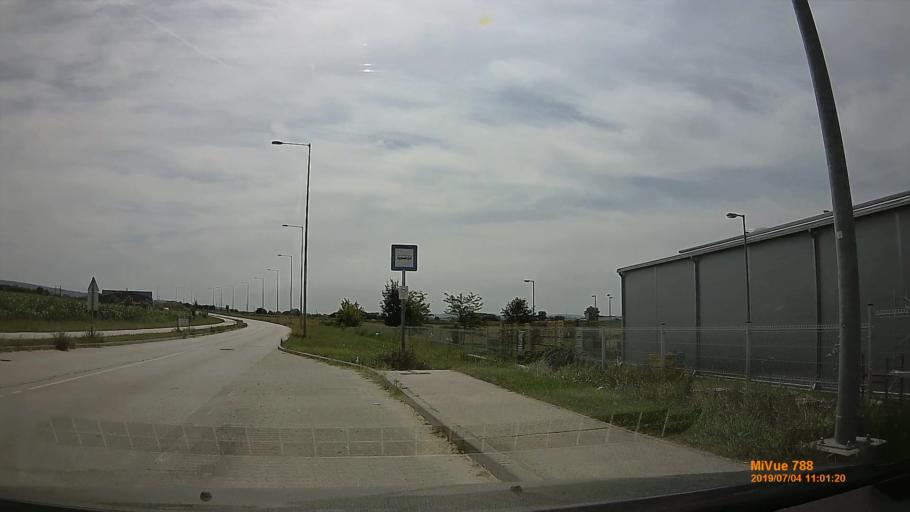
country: HU
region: Komarom-Esztergom
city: Tata
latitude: 47.6305
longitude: 18.2965
